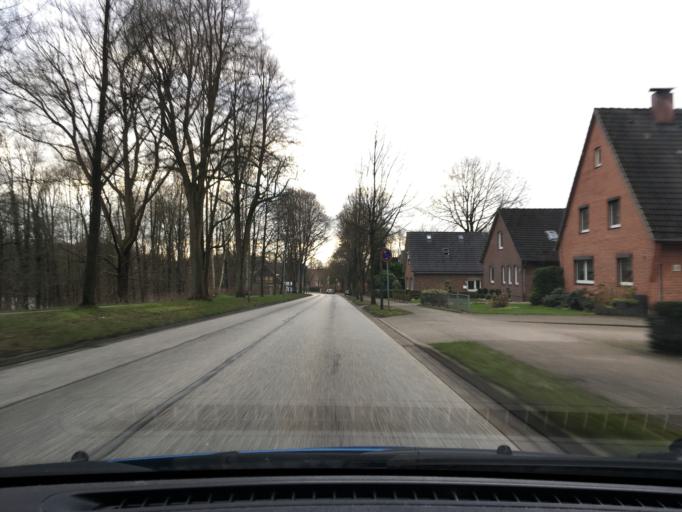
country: DE
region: Schleswig-Holstein
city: Ottenbuttel
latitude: 53.9484
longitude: 9.4944
